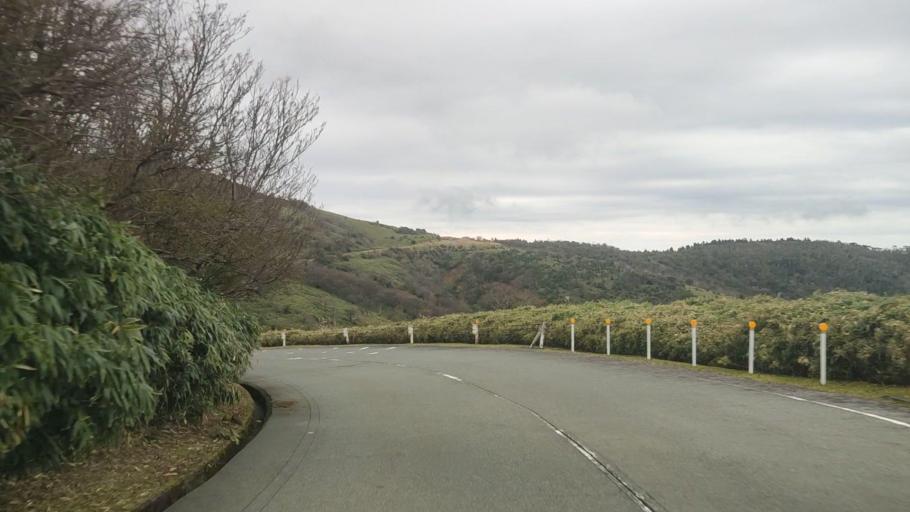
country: JP
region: Shizuoka
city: Heda
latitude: 34.9485
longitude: 138.8382
